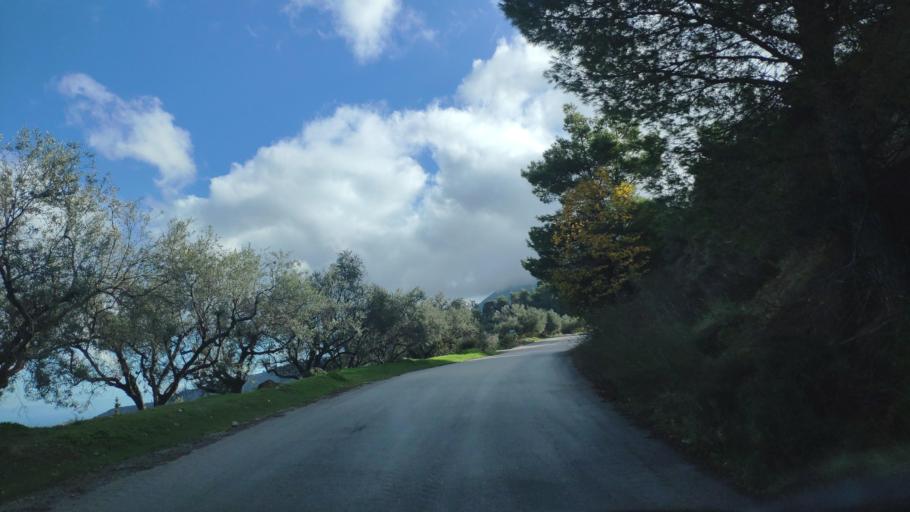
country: GR
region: West Greece
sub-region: Nomos Achaias
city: Aiyira
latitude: 38.1021
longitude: 22.4457
